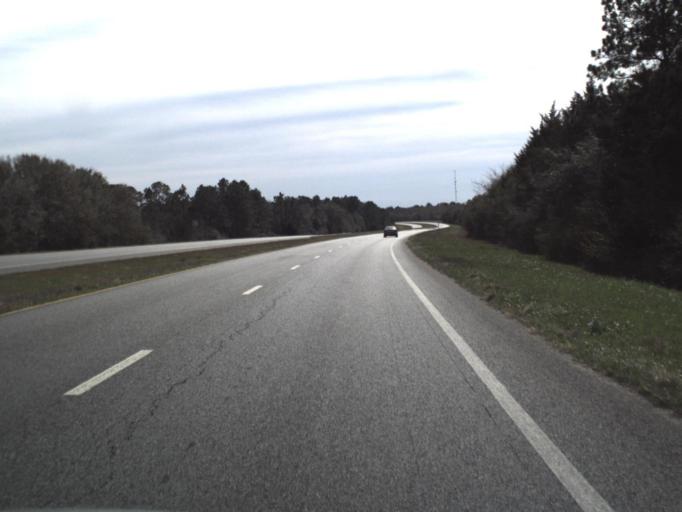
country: US
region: Florida
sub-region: Washington County
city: Chipley
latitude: 30.6117
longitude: -85.3963
